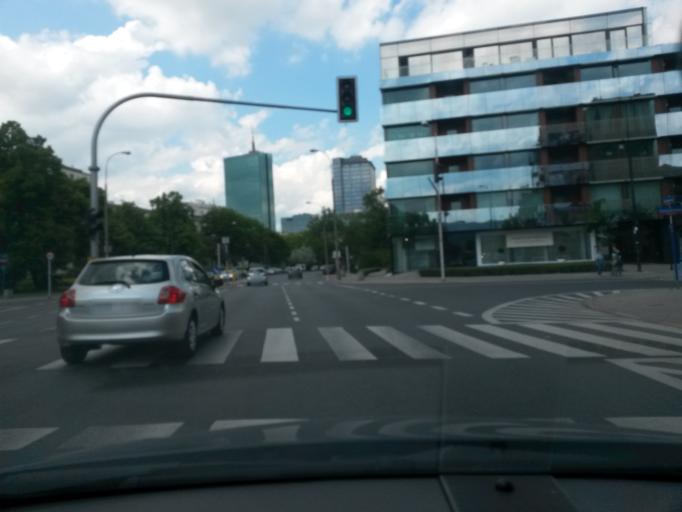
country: PL
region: Masovian Voivodeship
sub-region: Warszawa
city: Wola
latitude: 52.2516
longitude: 21.0025
